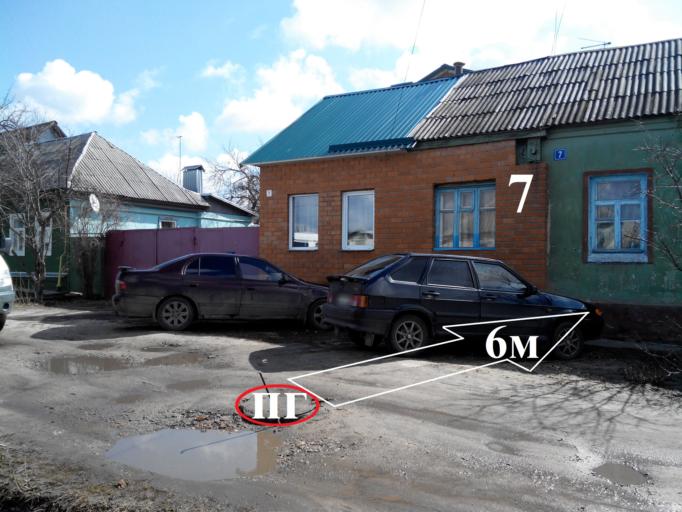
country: RU
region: Voronezj
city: Voronezh
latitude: 51.6315
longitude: 39.1706
